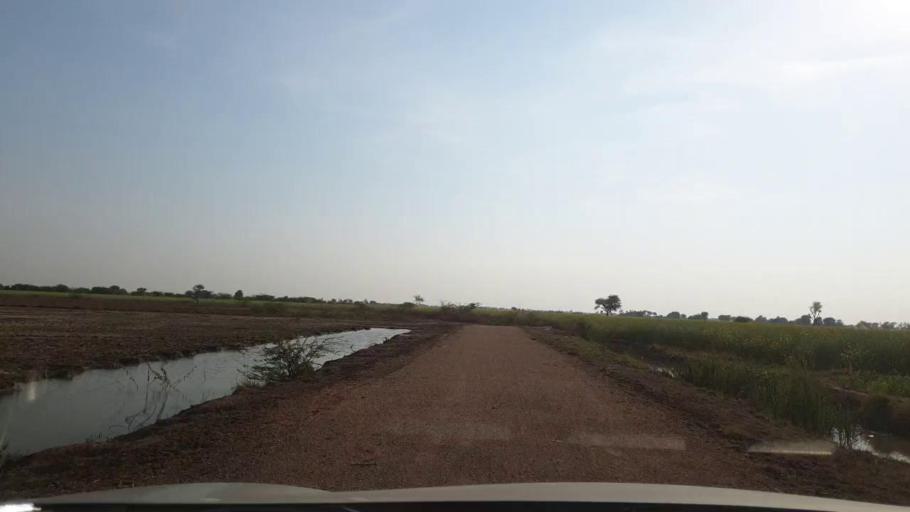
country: PK
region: Sindh
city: Berani
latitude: 25.7074
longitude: 68.8053
